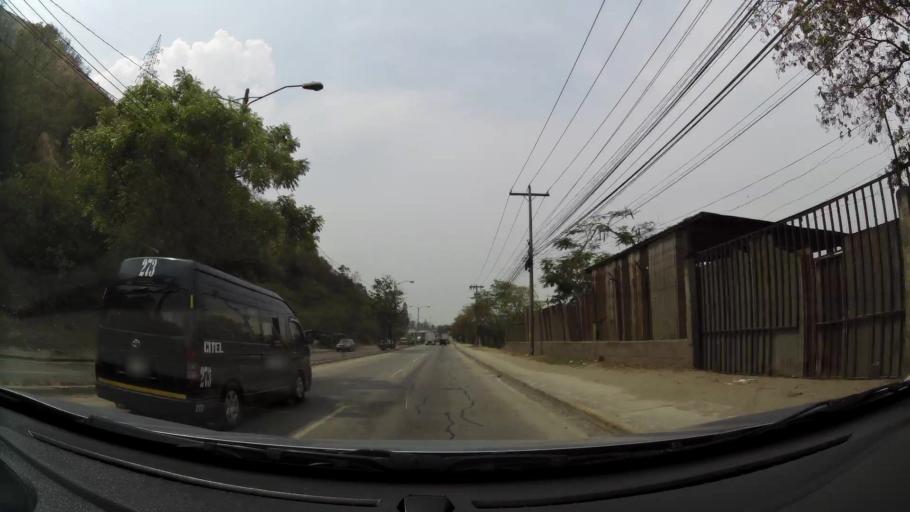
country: HN
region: Cortes
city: Chotepe
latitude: 15.4349
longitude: -88.0210
